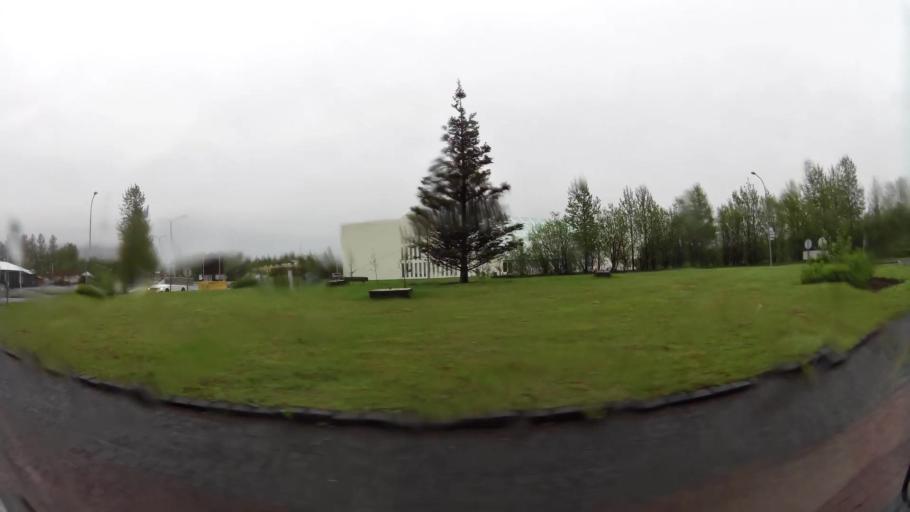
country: IS
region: South
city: Selfoss
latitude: 63.9315
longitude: -20.9994
